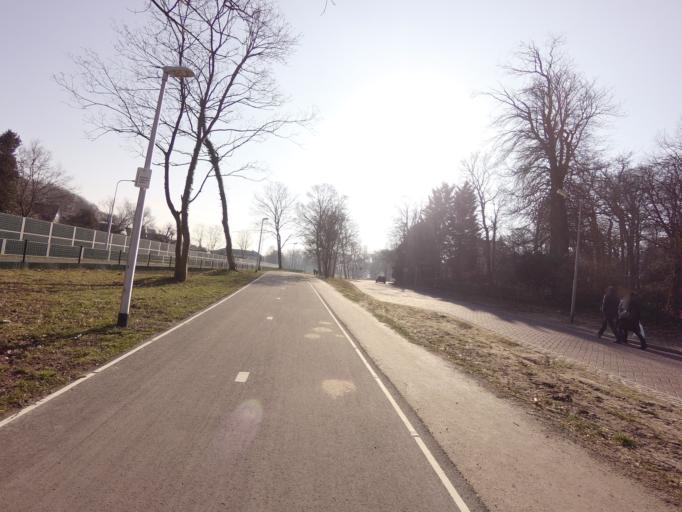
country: NL
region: North Holland
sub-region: Gemeente Velsen
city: Velsen-Zuid
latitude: 52.4442
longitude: 4.6323
